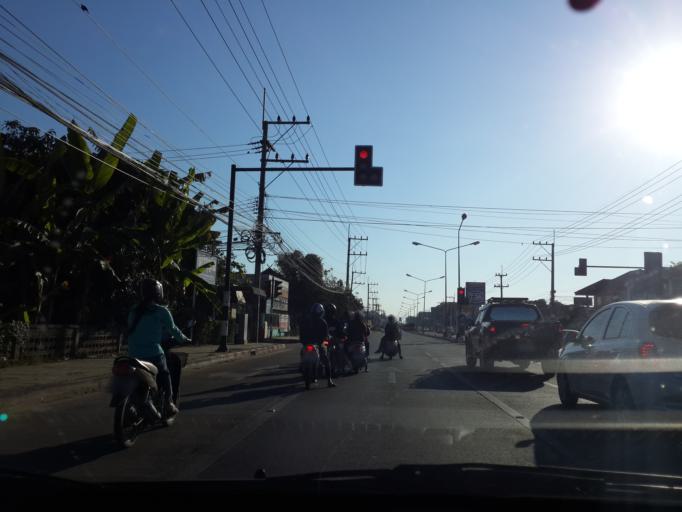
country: TH
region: Chiang Mai
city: Hang Dong
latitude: 18.7044
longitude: 98.9331
